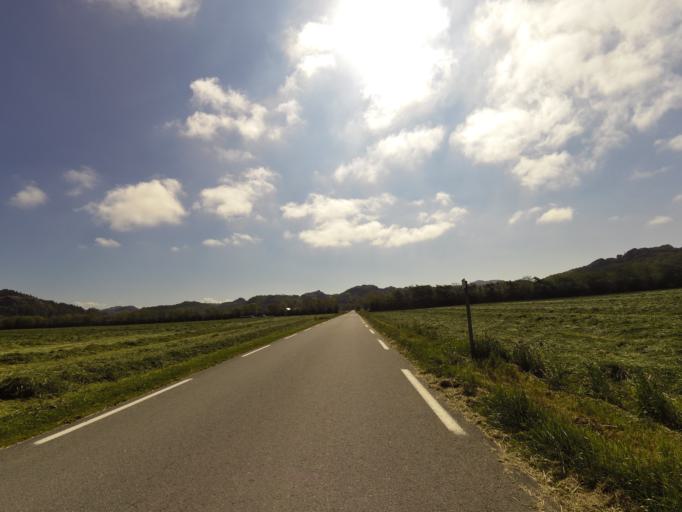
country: NO
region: Rogaland
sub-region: Ha
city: Vigrestad
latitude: 58.5196
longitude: 5.8133
